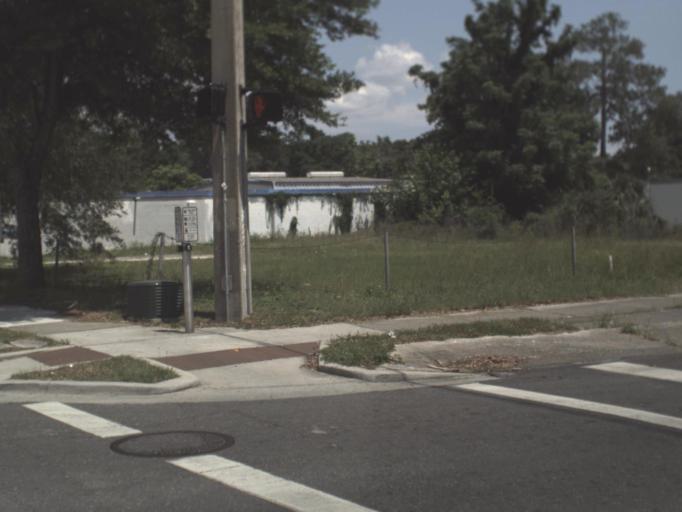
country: US
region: Florida
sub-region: Alachua County
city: Gainesville
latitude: 29.6519
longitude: -82.3147
